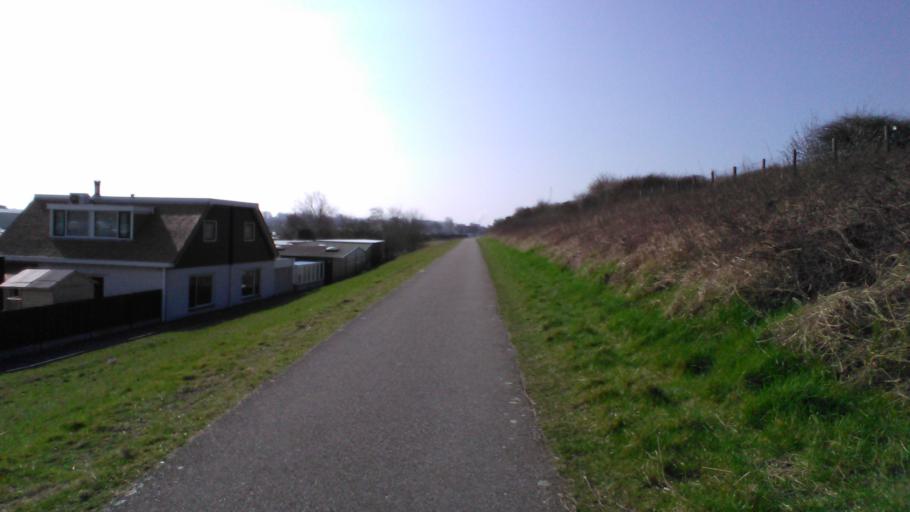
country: NL
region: South Holland
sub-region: Gemeente Rotterdam
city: Hoek van Holland
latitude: 51.9967
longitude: 4.1302
